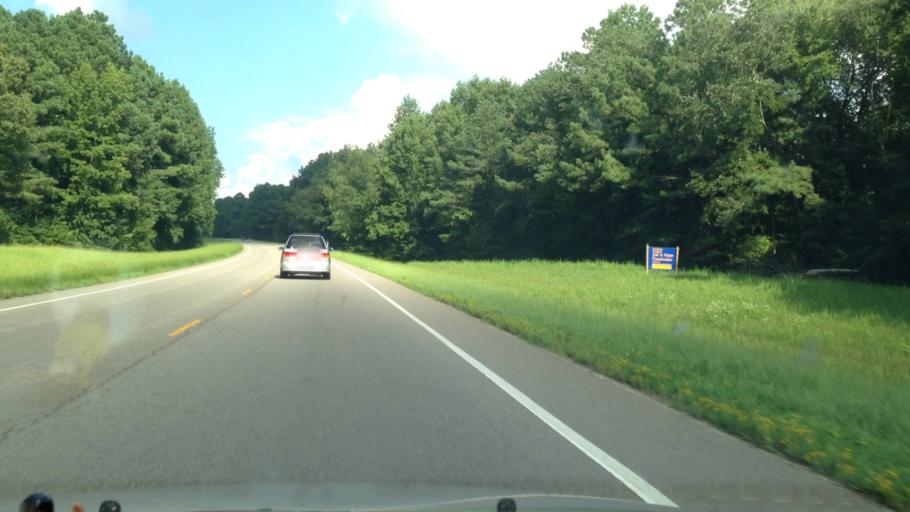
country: US
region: North Carolina
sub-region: Lee County
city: Broadway
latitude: 35.4378
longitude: -79.0627
